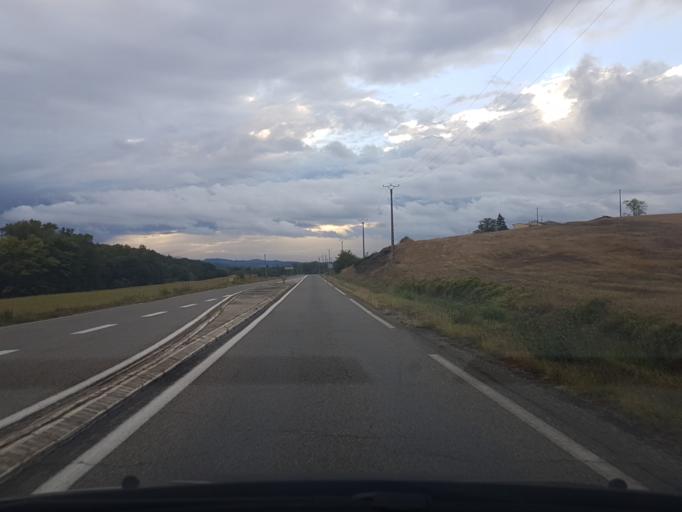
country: FR
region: Midi-Pyrenees
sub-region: Departement de l'Ariege
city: Mirepoix
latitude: 43.1038
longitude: 1.9164
